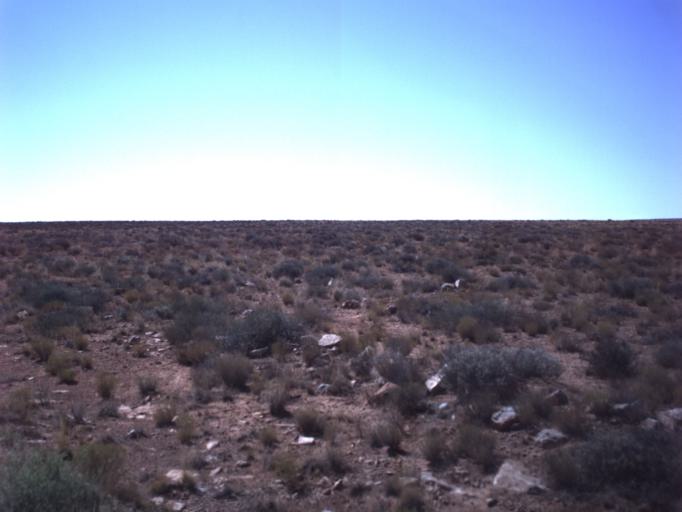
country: US
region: Arizona
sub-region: Navajo County
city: Kayenta
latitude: 37.1812
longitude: -109.9223
